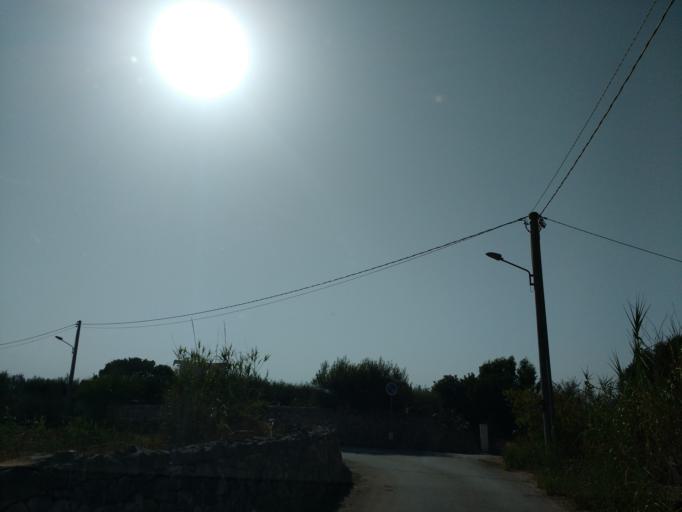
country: IT
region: Sicily
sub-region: Ragusa
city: Cava d'Aliga
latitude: 36.7319
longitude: 14.6928
